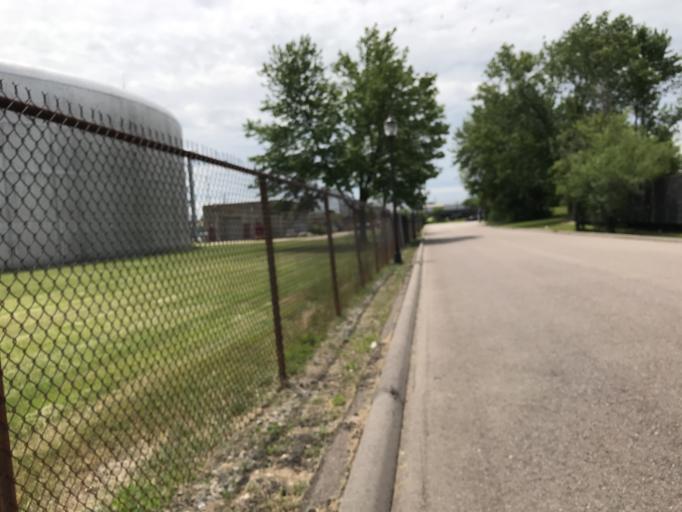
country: US
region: Michigan
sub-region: Oakland County
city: Bingham Farms
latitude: 42.5025
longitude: -83.2875
